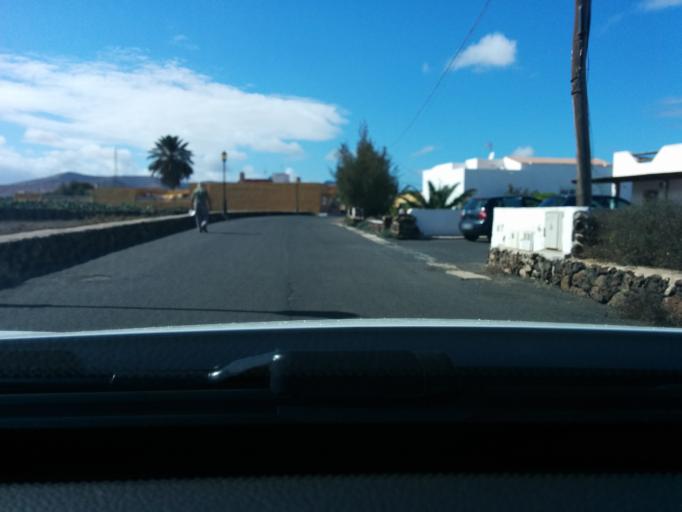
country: ES
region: Canary Islands
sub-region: Provincia de Las Palmas
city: La Oliva
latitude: 28.6308
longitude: -13.9018
